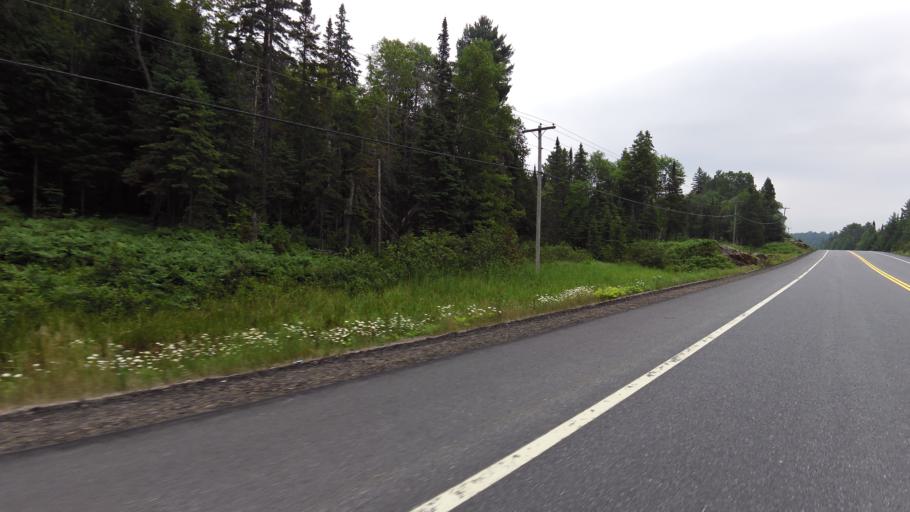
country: CA
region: Ontario
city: Huntsville
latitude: 45.4681
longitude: -78.7859
